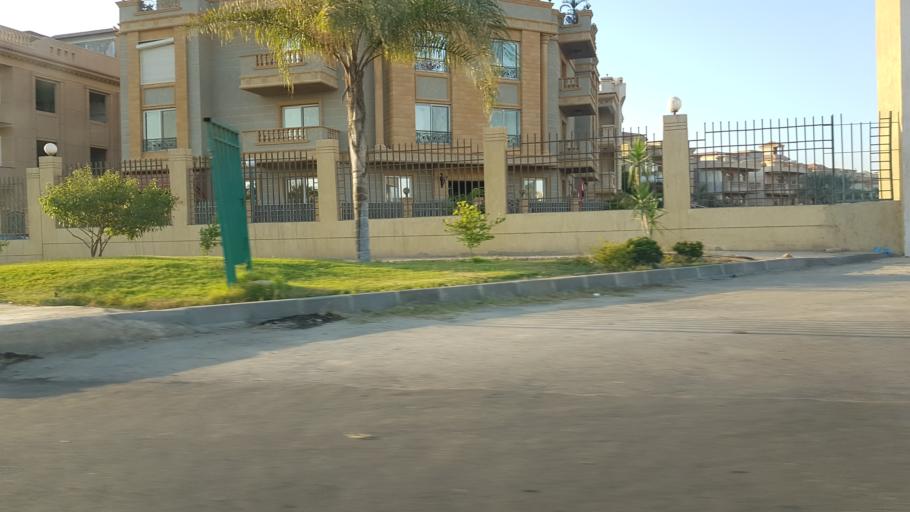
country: EG
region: Muhafazat al Qalyubiyah
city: Al Khankah
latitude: 30.0621
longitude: 31.4388
